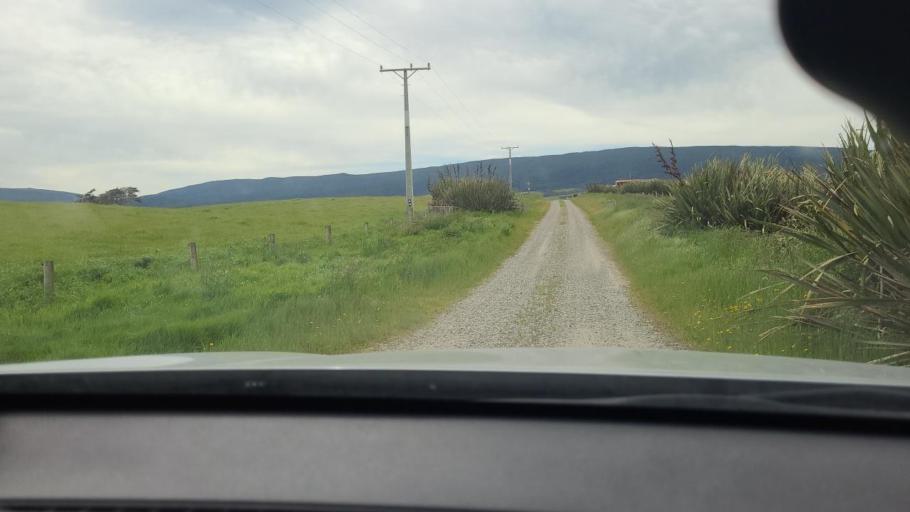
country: NZ
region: Southland
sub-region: Southland District
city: Riverton
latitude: -46.2713
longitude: 167.7291
